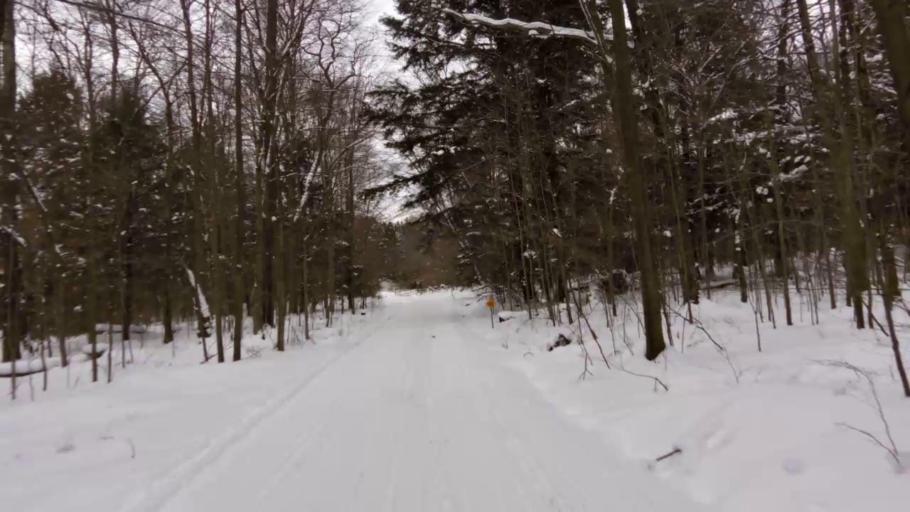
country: US
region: Pennsylvania
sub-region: McKean County
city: Bradford
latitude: 42.0202
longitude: -78.7224
